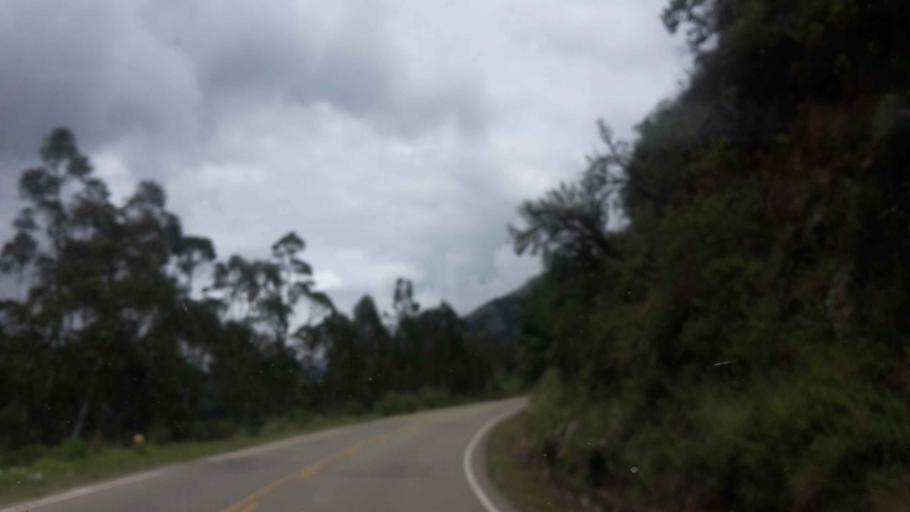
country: BO
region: Cochabamba
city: Totora
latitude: -17.4996
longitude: -65.4302
